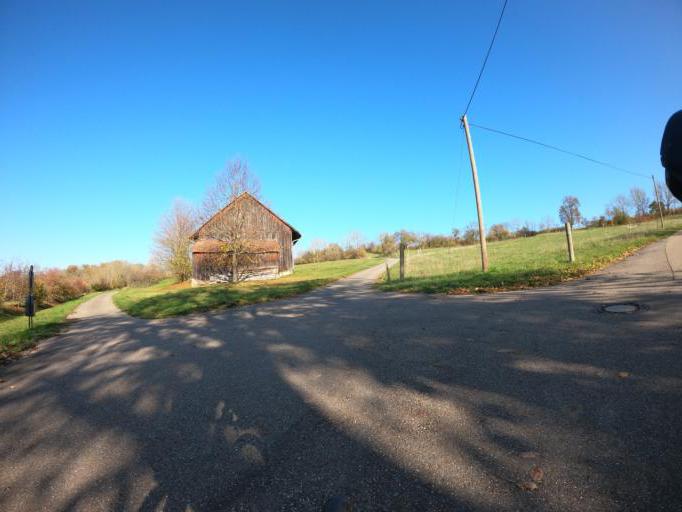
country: DE
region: Baden-Wuerttemberg
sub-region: Regierungsbezirk Stuttgart
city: Weil der Stadt
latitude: 48.7287
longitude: 8.8961
